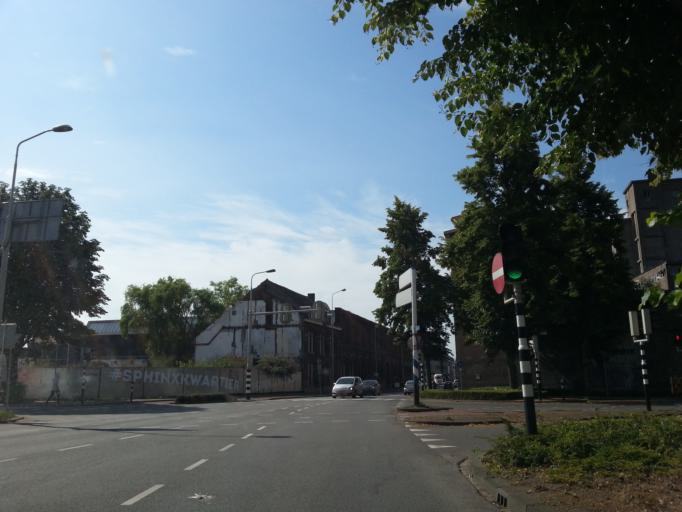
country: NL
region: Limburg
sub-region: Gemeente Maastricht
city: Maastricht
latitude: 50.8581
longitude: 5.6900
